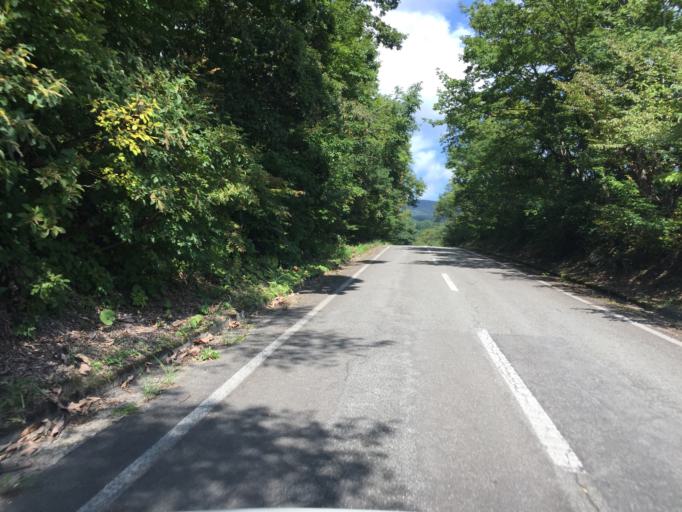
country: JP
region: Fukushima
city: Inawashiro
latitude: 37.5841
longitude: 140.0268
